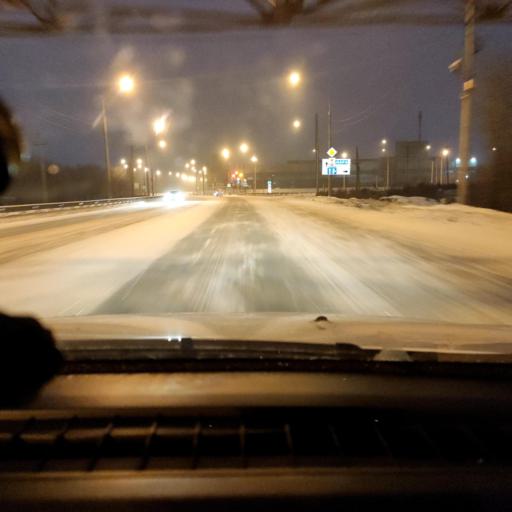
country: RU
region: Samara
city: Otradnyy
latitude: 53.3742
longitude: 51.3719
